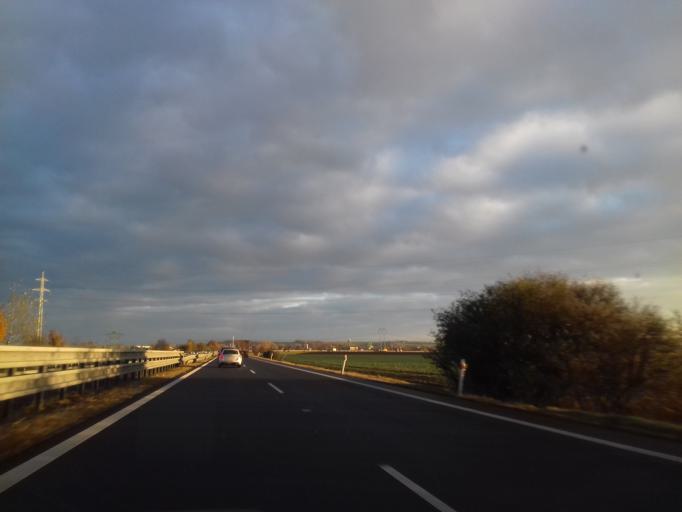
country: CZ
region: Olomoucky
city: Lutin
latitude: 49.5178
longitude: 17.1503
